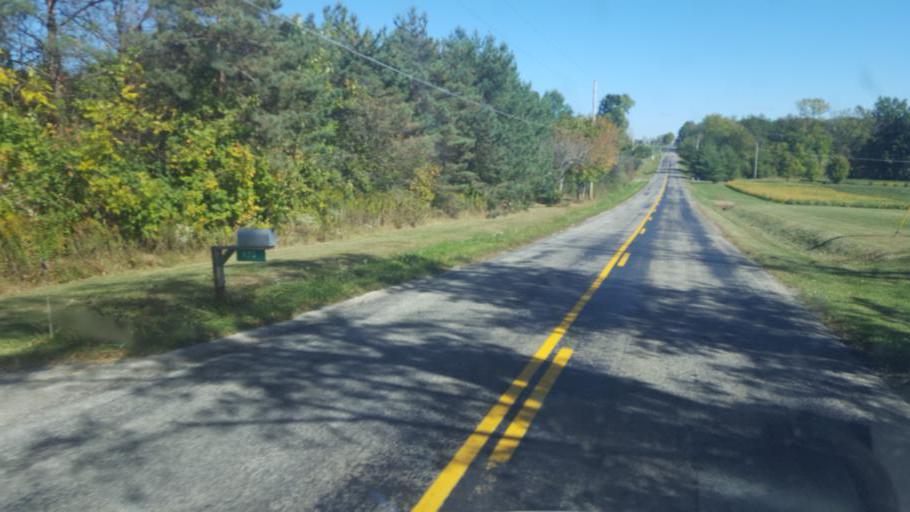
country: US
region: Ohio
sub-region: Ashland County
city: Ashland
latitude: 40.9929
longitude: -82.3157
